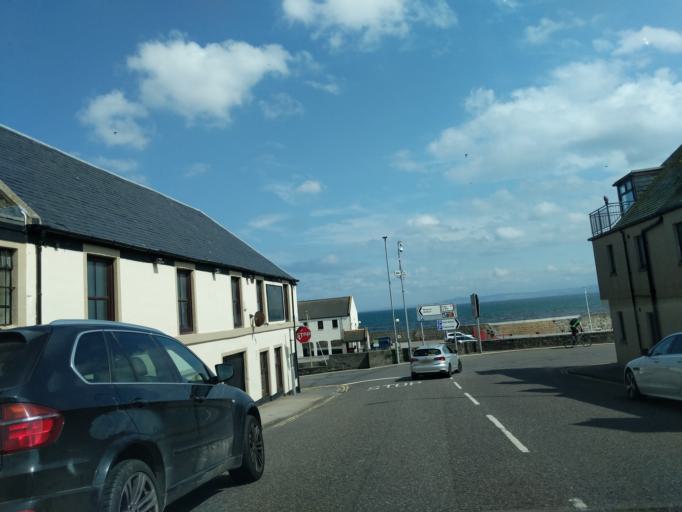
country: GB
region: Scotland
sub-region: Moray
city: Lossiemouth
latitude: 57.7221
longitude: -3.2807
